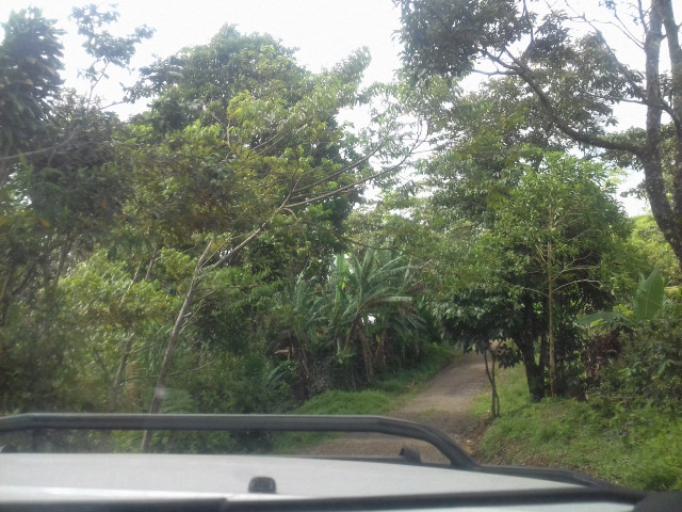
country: NI
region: Atlantico Norte (RAAN)
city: Waslala
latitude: 13.2182
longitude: -85.5739
